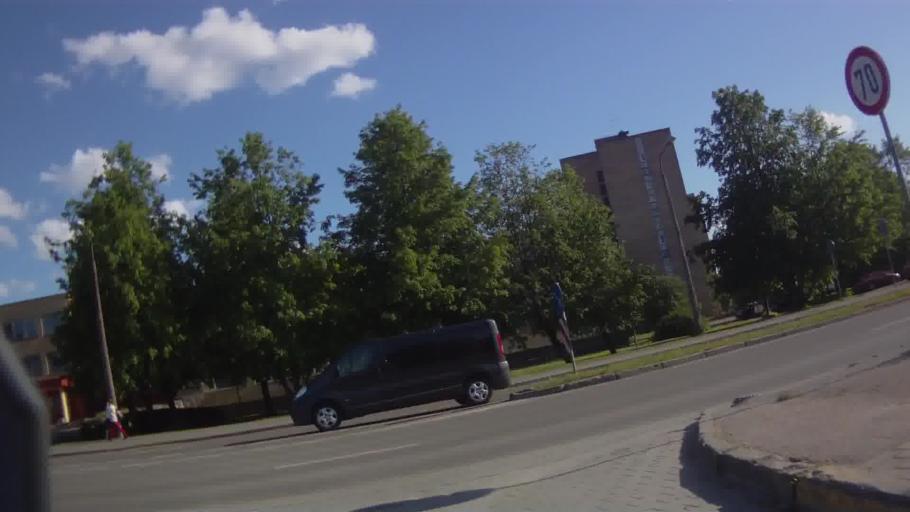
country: LV
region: Riga
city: Riga
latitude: 56.9759
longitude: 24.1325
